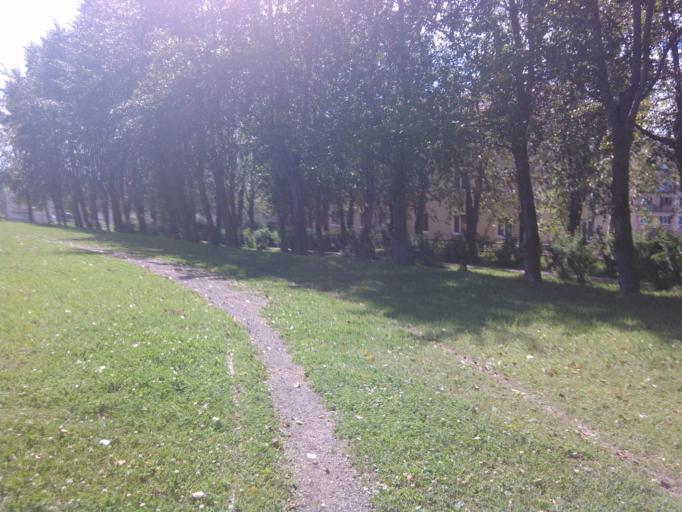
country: RU
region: Sverdlovsk
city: Krasnotur'insk
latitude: 59.7603
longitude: 60.1896
